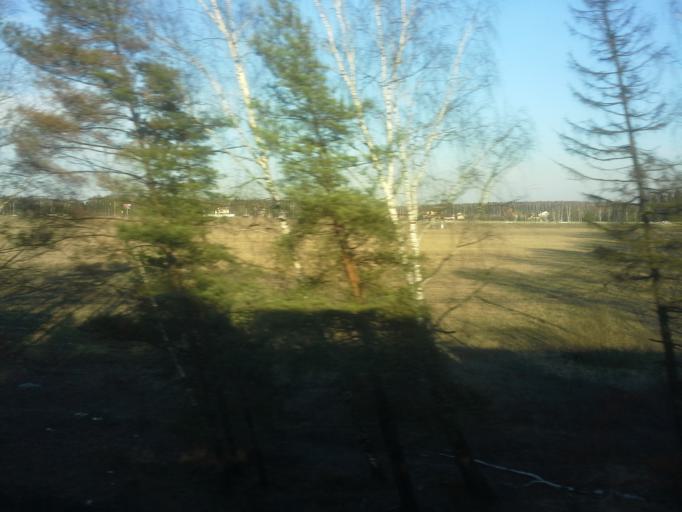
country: RU
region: Moskovskaya
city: Nekrasovskiy
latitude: 56.1062
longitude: 37.5141
